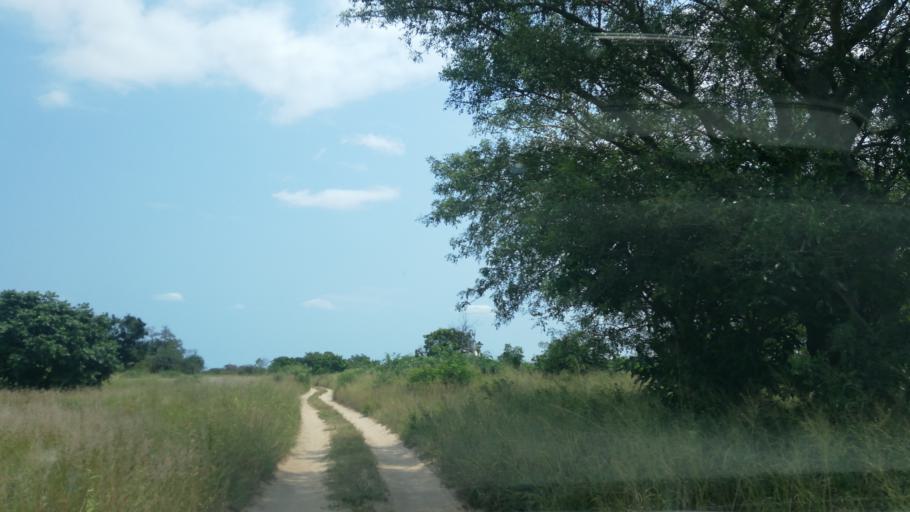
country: MZ
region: Maputo
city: Matola
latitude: -26.1102
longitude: 32.4233
